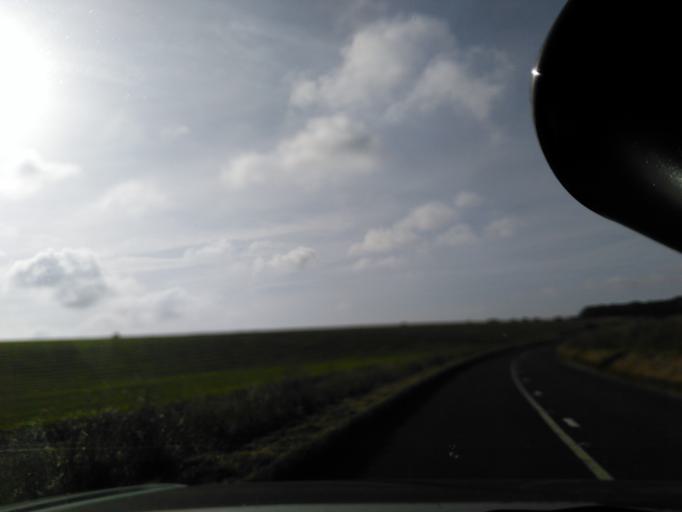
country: GB
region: England
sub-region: Wiltshire
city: Market Lavington
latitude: 51.2345
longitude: -1.9682
